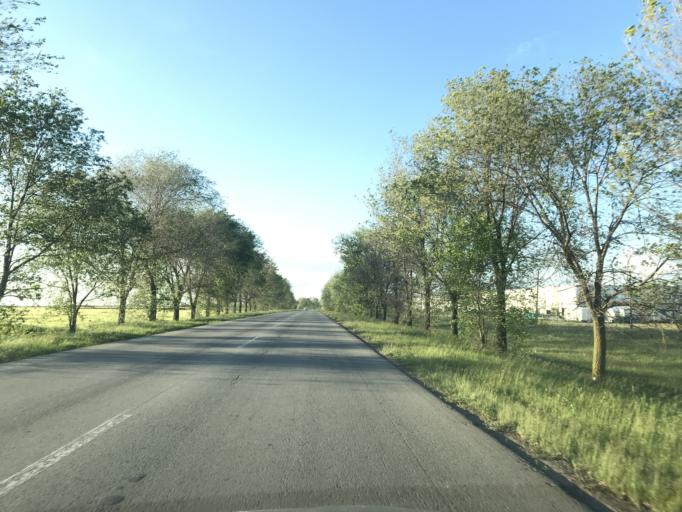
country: RS
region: Autonomna Pokrajina Vojvodina
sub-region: Srednjebanatski Okrug
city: Zrenjanin
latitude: 45.3855
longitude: 20.3520
